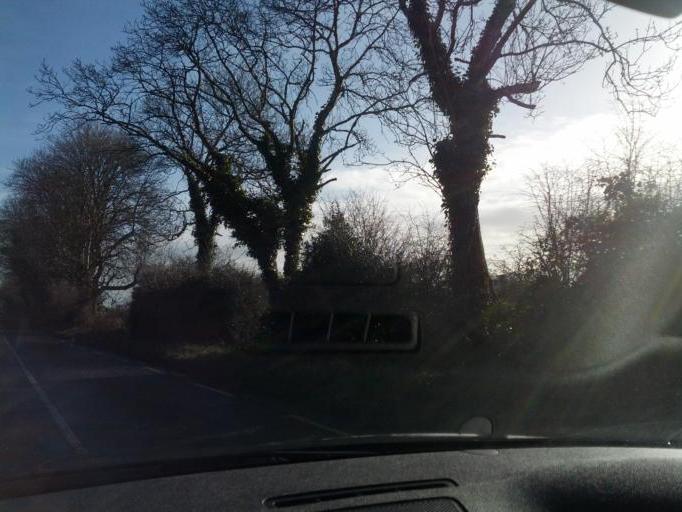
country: IE
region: Connaught
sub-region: County Galway
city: Athenry
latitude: 53.4029
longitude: -8.6438
